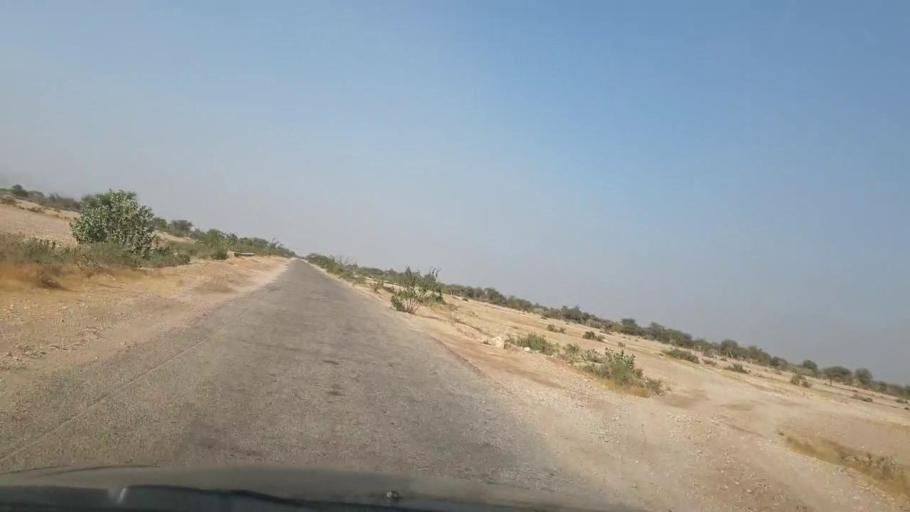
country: PK
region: Sindh
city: Jamshoro
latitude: 25.5540
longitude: 67.8290
